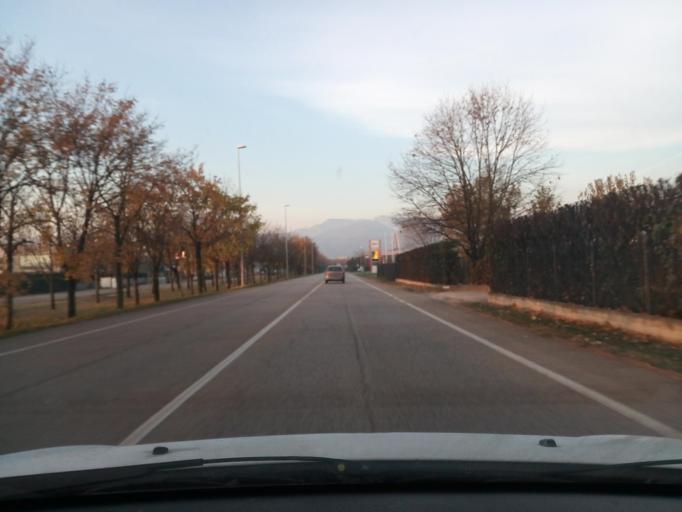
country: IT
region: Veneto
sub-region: Provincia di Vicenza
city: Zane
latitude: 45.7243
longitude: 11.4189
